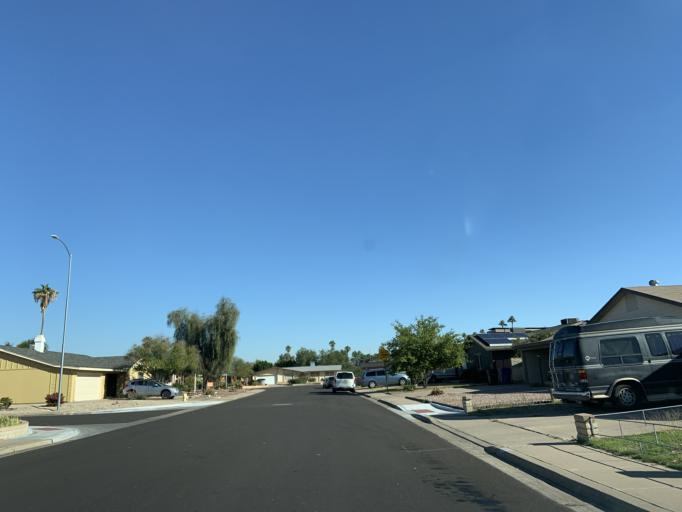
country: US
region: Arizona
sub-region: Maricopa County
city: Tempe
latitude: 33.4019
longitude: -111.8805
